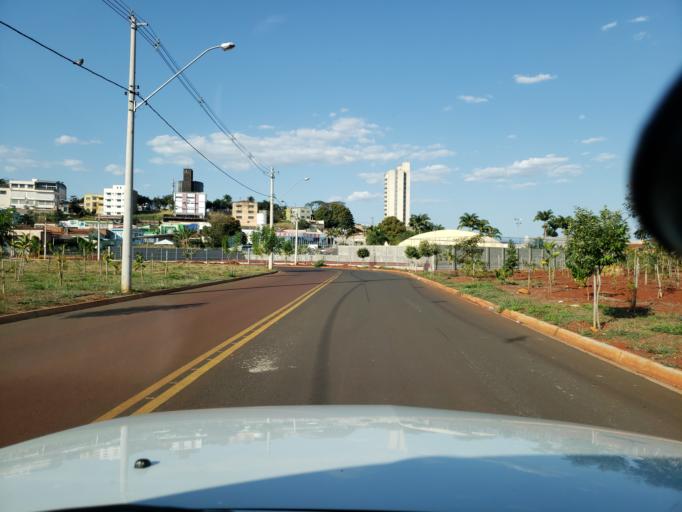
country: BR
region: Sao Paulo
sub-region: Moji-Guacu
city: Mogi-Gaucu
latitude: -22.3700
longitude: -46.9476
